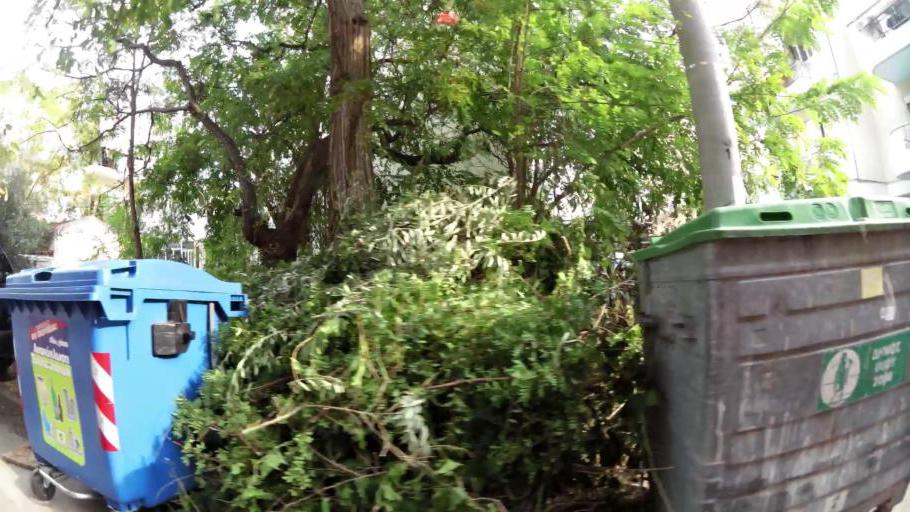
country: GR
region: Attica
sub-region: Nomarchia Athinas
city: Ilion
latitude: 38.0259
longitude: 23.6984
